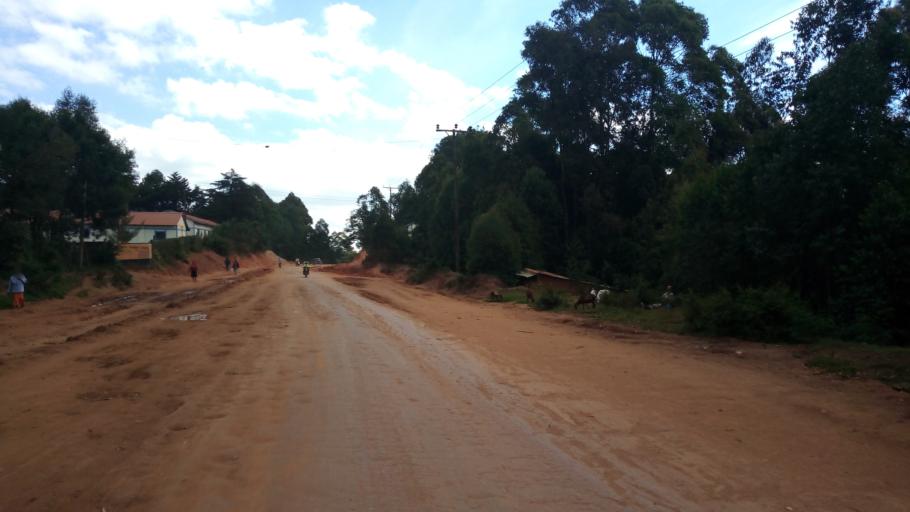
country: KE
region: Makueni
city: Wote
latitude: -1.6577
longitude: 37.4524
